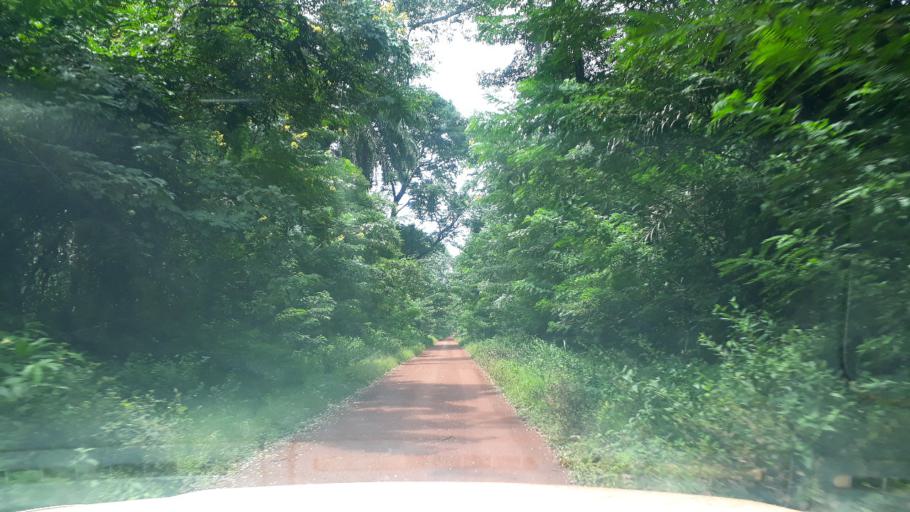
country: CD
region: Eastern Province
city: Aketi
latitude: 2.9284
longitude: 24.0873
